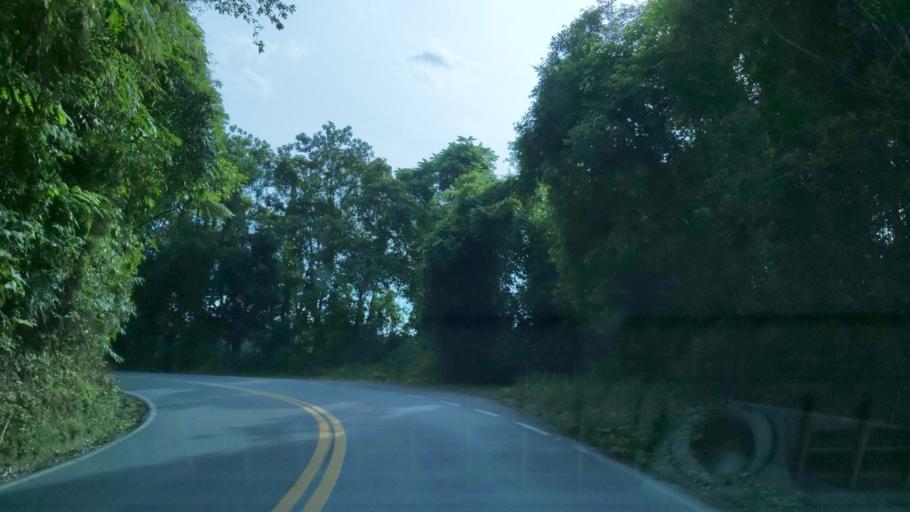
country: BR
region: Sao Paulo
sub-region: Juquia
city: Juquia
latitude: -24.1079
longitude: -47.6247
